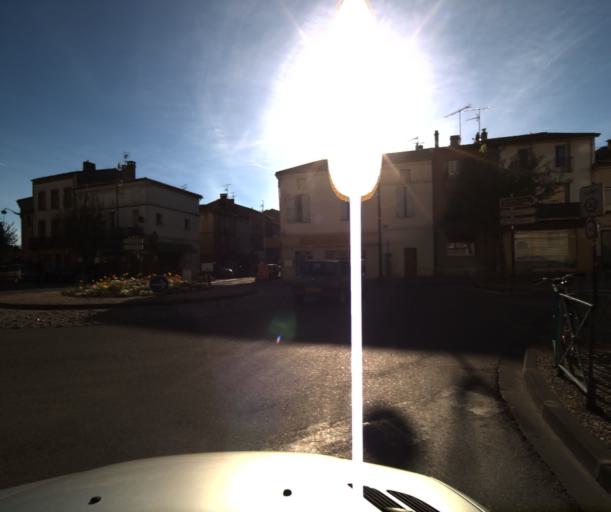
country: FR
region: Midi-Pyrenees
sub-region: Departement du Tarn-et-Garonne
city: Moissac
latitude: 44.1043
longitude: 1.0882
